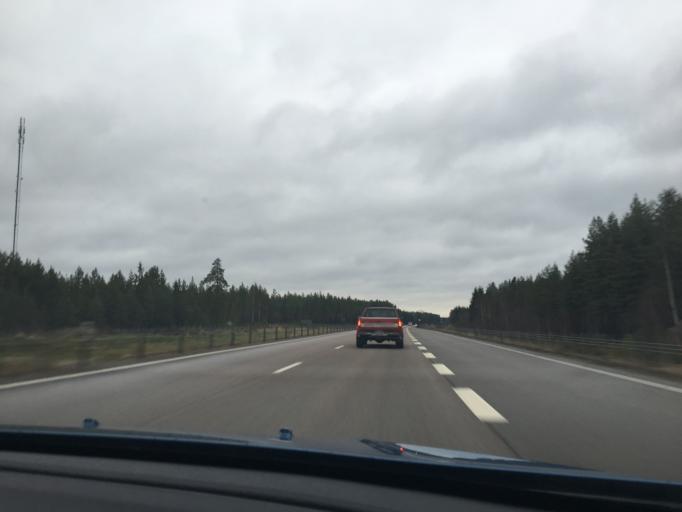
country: SE
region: Uppsala
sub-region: Alvkarleby Kommun
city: AElvkarleby
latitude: 60.4422
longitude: 17.4193
